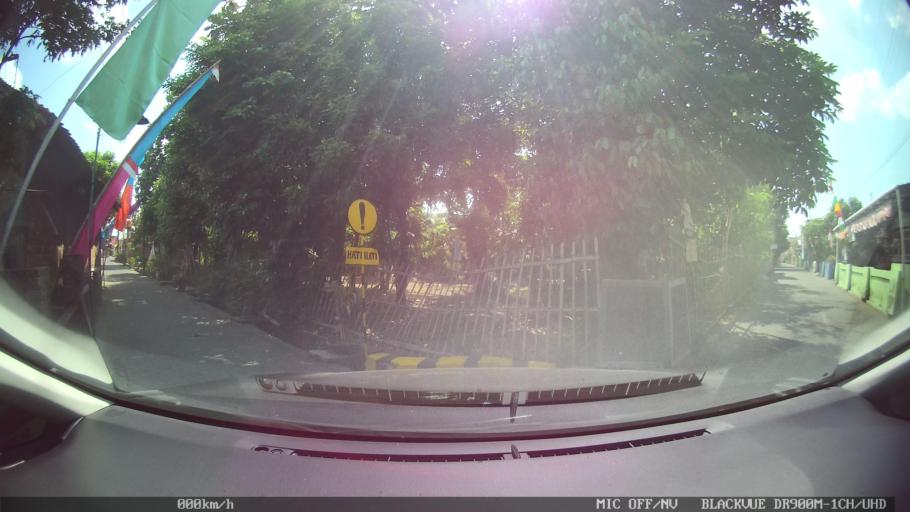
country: ID
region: Daerah Istimewa Yogyakarta
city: Kasihan
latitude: -7.8344
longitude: 110.3722
